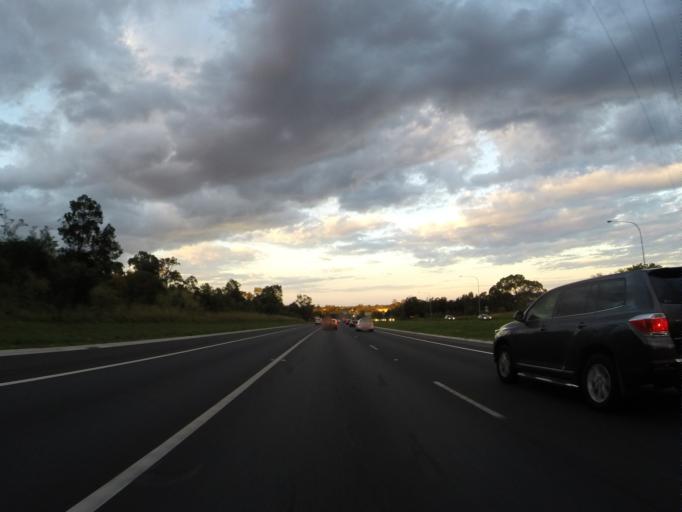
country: AU
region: New South Wales
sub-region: Campbelltown Municipality
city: Campbelltown
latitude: -34.0578
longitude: 150.7929
